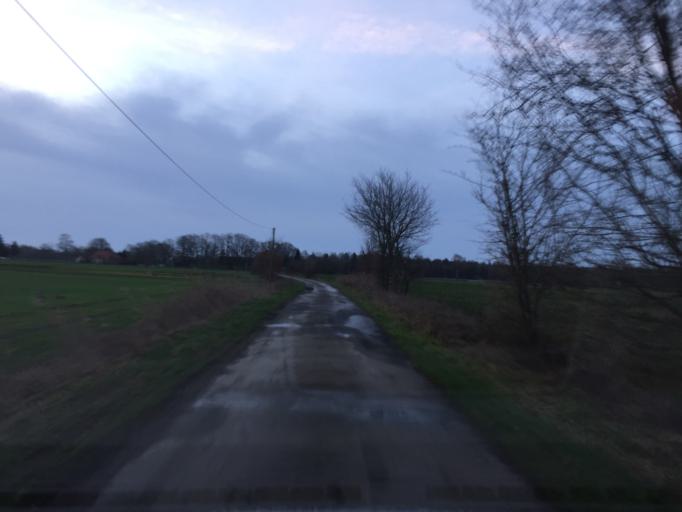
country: DE
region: Lower Saxony
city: Kirchdorf
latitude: 52.6094
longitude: 8.8707
